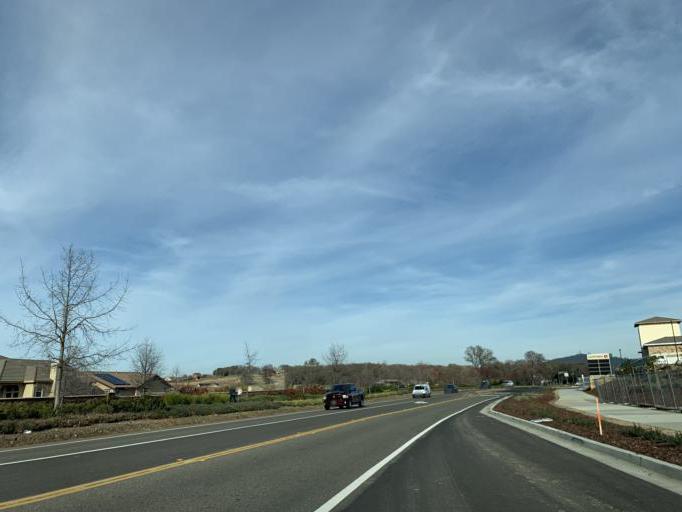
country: US
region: California
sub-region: El Dorado County
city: Cameron Park
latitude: 38.6749
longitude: -121.0306
